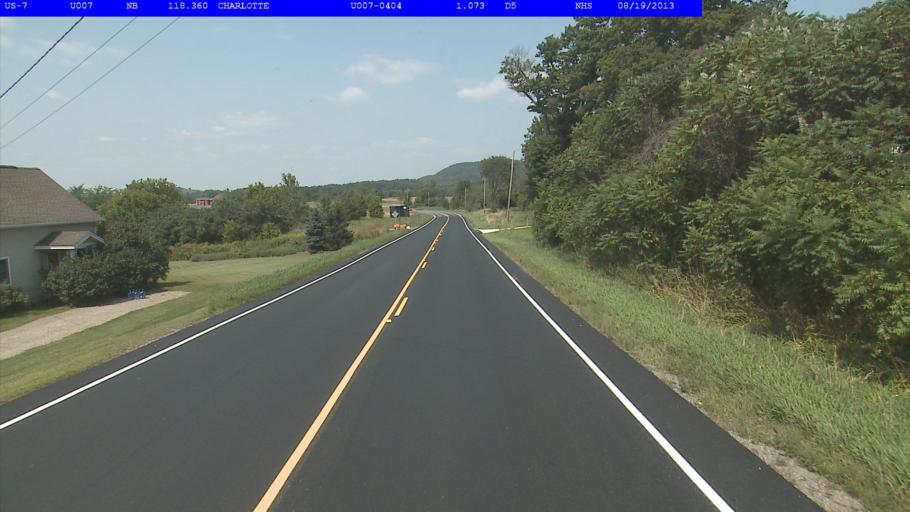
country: US
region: Vermont
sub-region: Addison County
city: Vergennes
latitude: 44.2776
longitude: -73.2350
